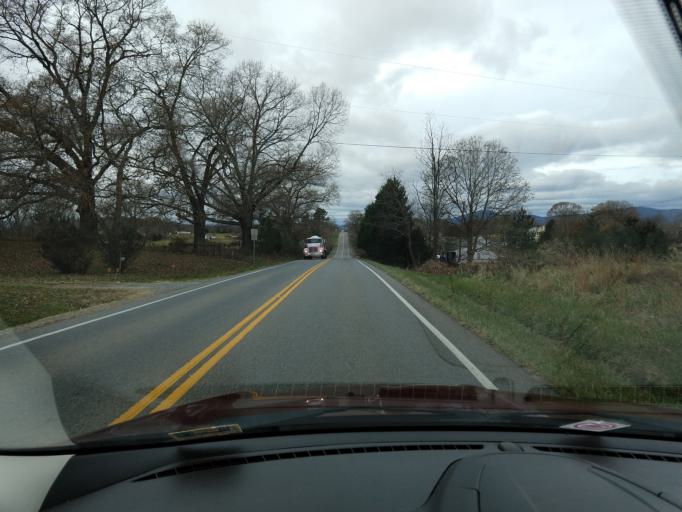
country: US
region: Virginia
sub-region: Botetourt County
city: Blue Ridge
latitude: 37.2527
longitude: -79.7057
